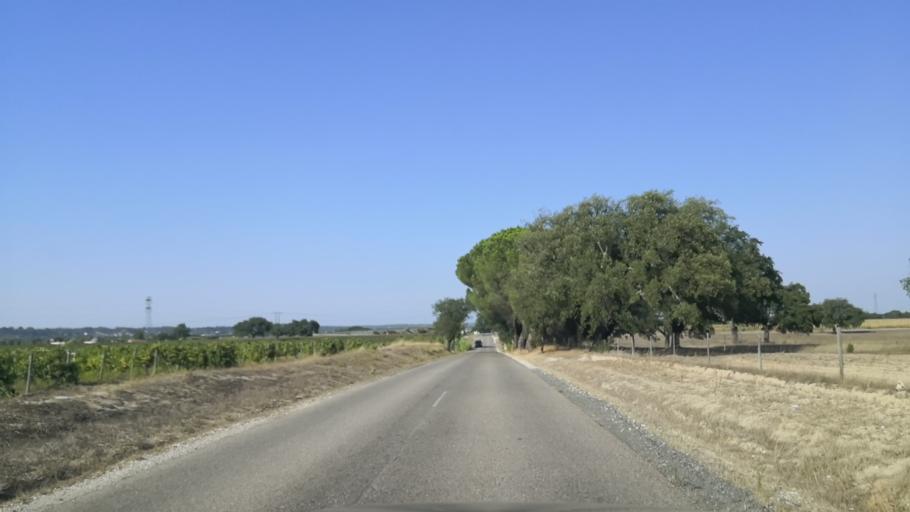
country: PT
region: Santarem
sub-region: Coruche
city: Coruche
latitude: 38.9317
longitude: -8.5193
